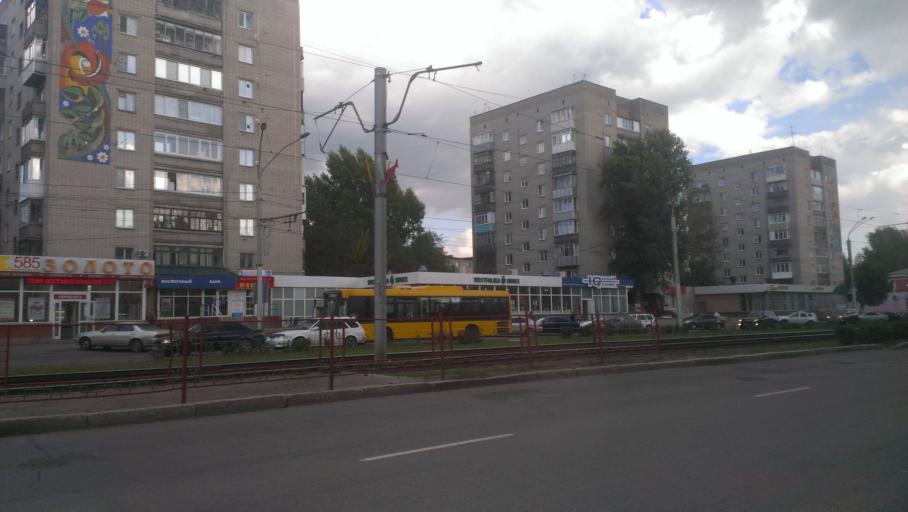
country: RU
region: Altai Krai
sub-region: Gorod Barnaulskiy
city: Barnaul
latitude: 53.3602
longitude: 83.7637
